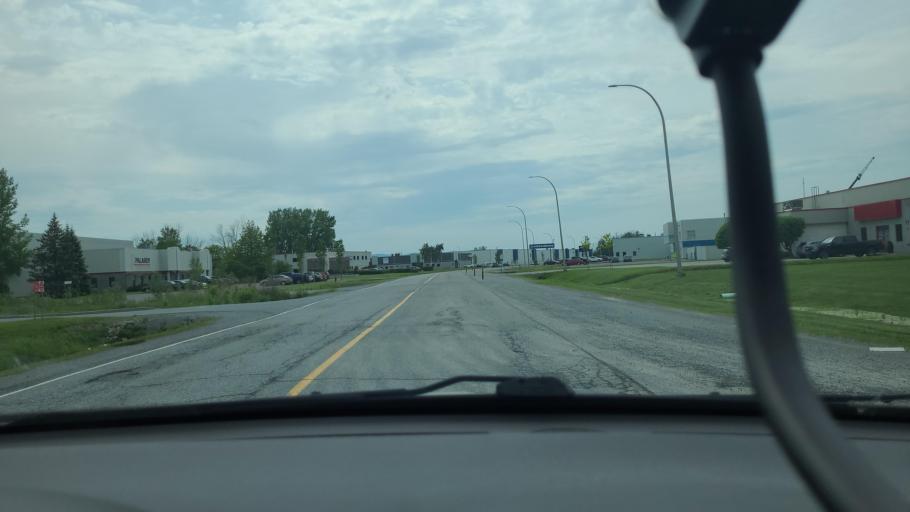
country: CA
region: Quebec
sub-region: Monteregie
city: Saint-Hyacinthe
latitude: 45.6301
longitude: -72.9871
